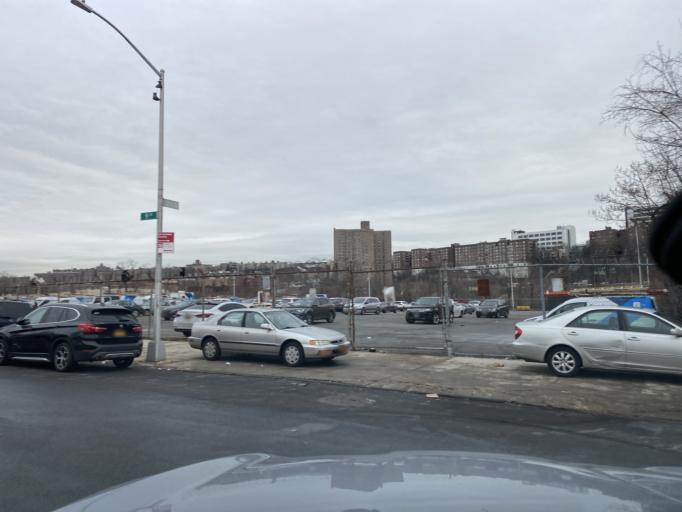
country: US
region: New York
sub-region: New York County
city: Inwood
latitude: 40.8704
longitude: -73.9122
